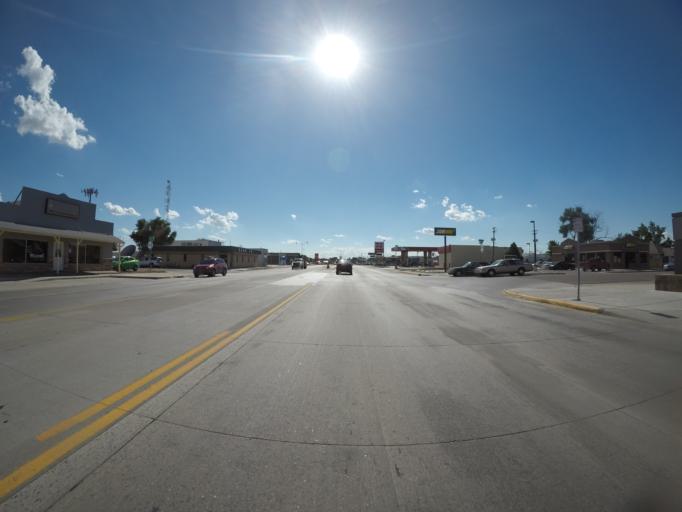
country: US
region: Colorado
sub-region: Logan County
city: Sterling
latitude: 40.6253
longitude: -103.2232
